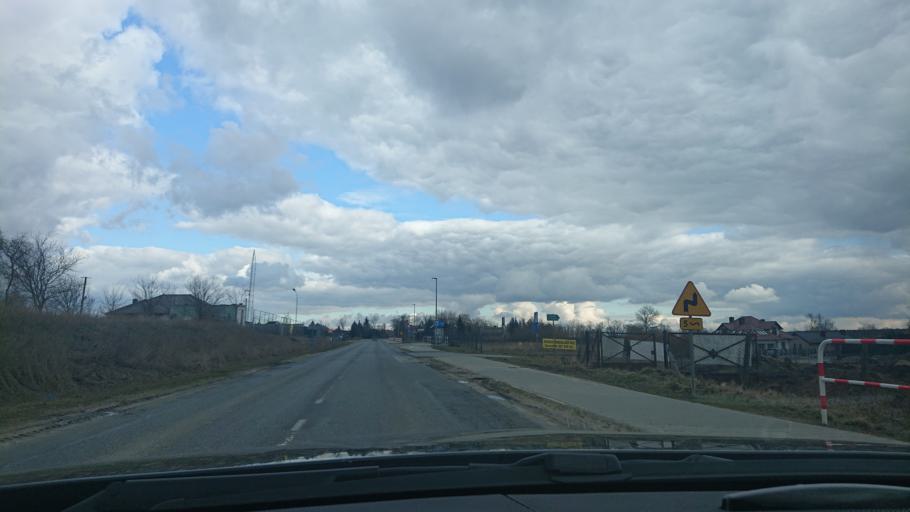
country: PL
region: Greater Poland Voivodeship
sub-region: Powiat gnieznienski
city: Gniezno
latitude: 52.5439
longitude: 17.6571
